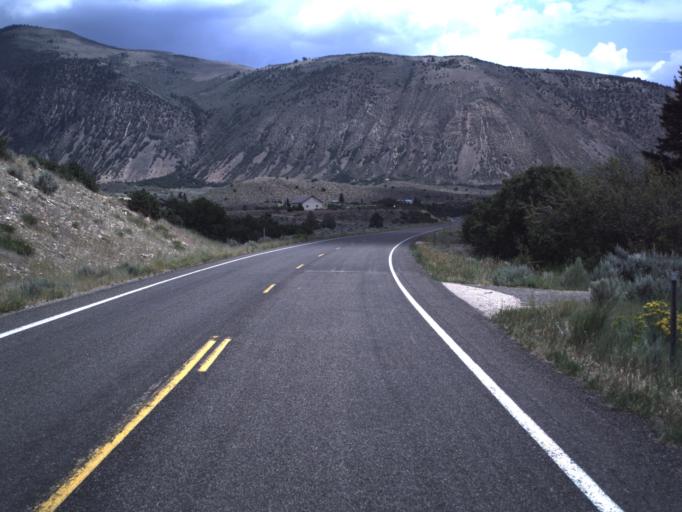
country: US
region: Utah
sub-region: Summit County
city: Francis
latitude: 40.4621
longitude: -110.8410
